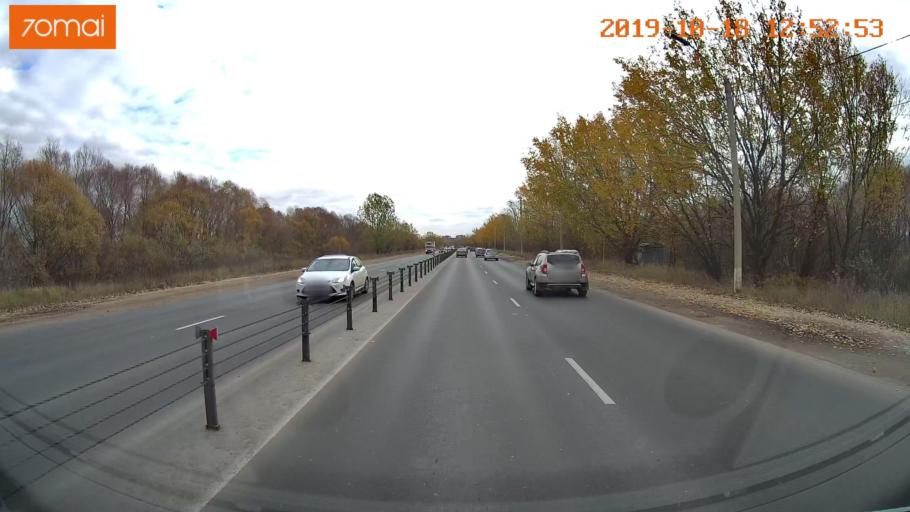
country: RU
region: Rjazan
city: Ryazan'
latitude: 54.6487
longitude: 39.6993
